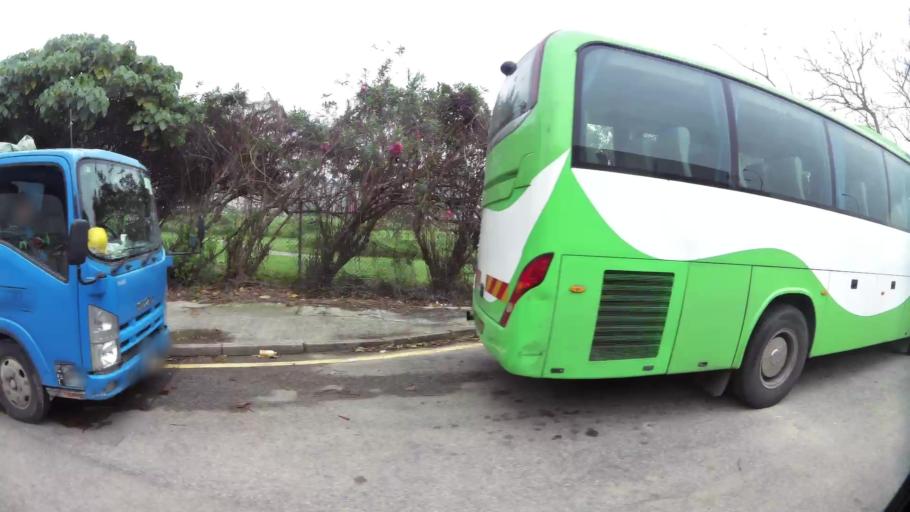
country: MO
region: Macau
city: Macau
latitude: 22.1382
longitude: 113.5578
